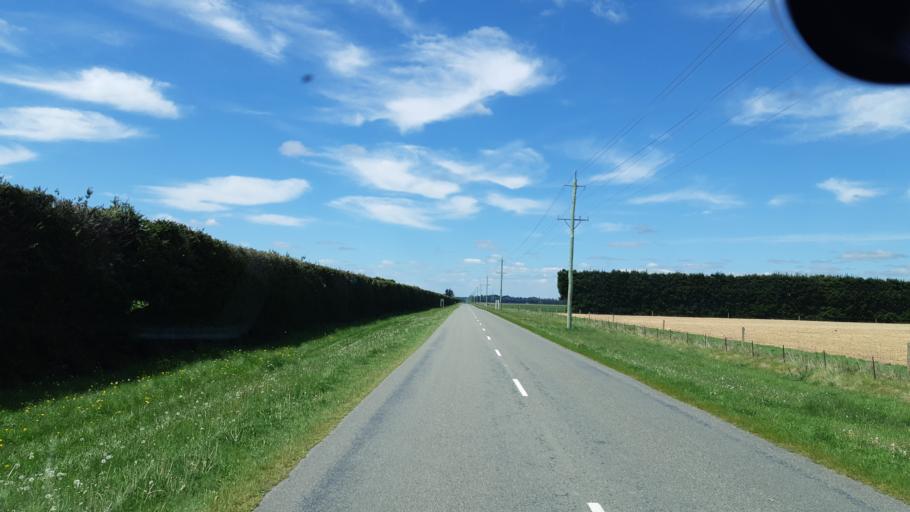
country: NZ
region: Canterbury
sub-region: Ashburton District
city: Methven
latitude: -43.7203
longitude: 171.4674
